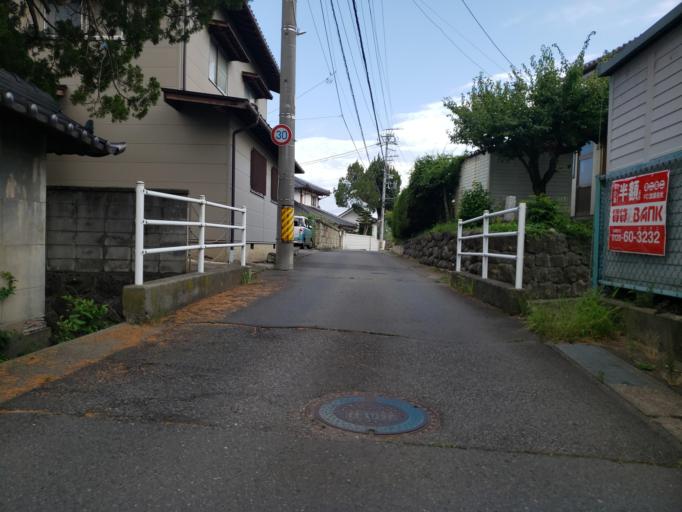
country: JP
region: Nagano
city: Nagano-shi
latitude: 36.6413
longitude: 138.1747
